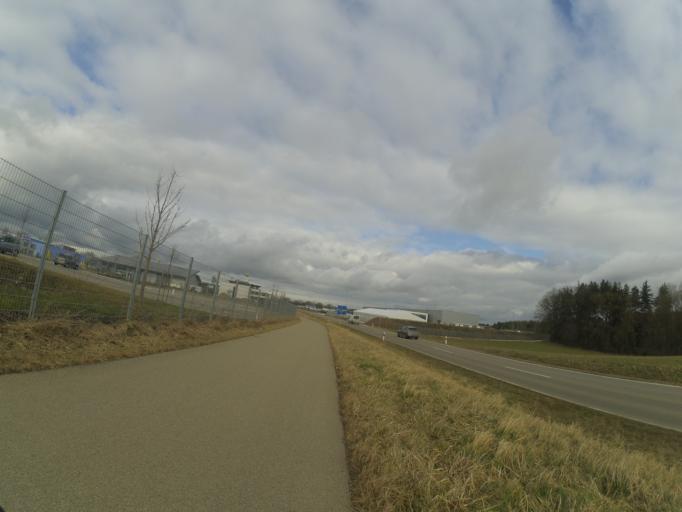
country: DE
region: Bavaria
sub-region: Swabia
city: Vohringen
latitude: 48.2831
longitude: 10.1178
